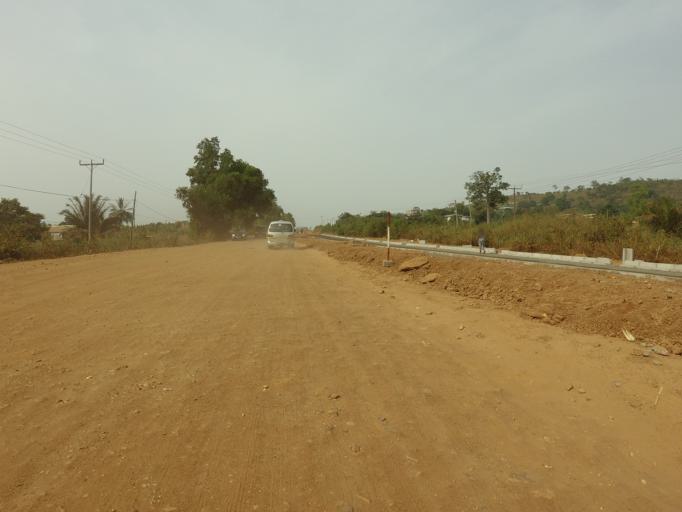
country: GH
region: Volta
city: Ho
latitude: 6.5952
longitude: 0.4416
